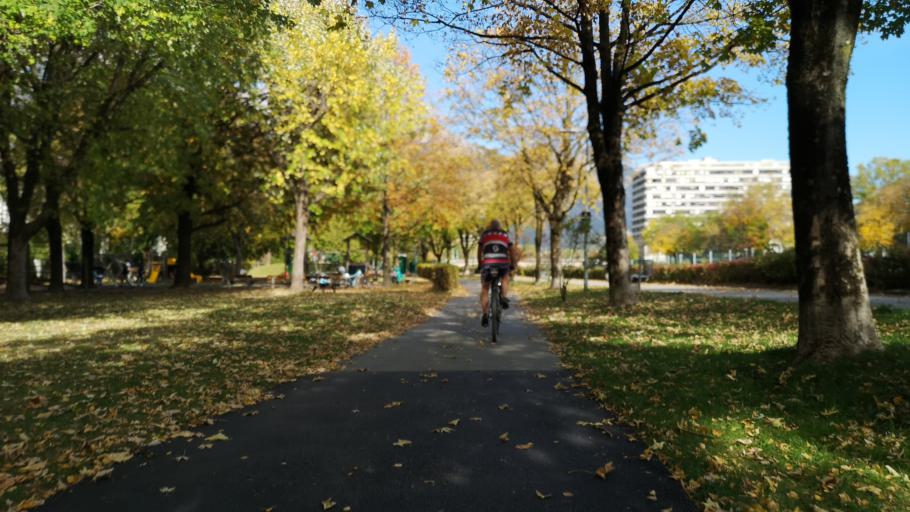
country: AT
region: Tyrol
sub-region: Innsbruck Stadt
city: Innsbruck
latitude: 47.2625
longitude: 11.3809
